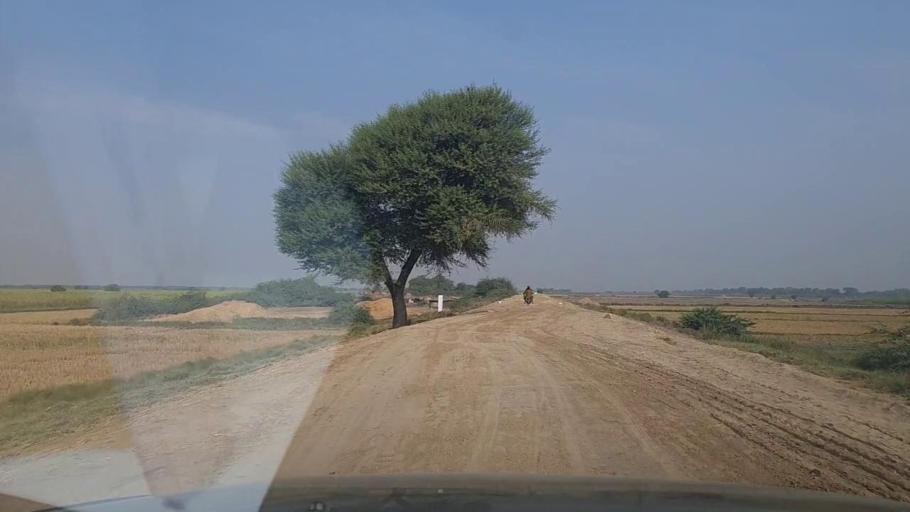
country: PK
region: Sindh
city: Bulri
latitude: 25.0103
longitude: 68.2860
